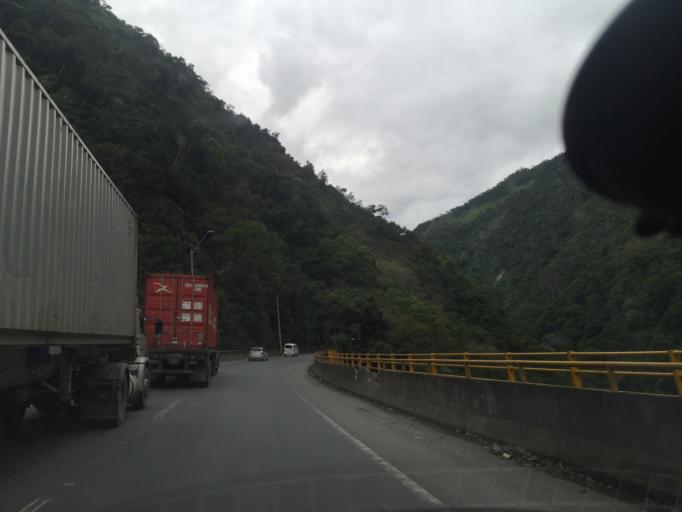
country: CO
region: Valle del Cauca
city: Dagua
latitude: 3.7734
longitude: -76.7415
